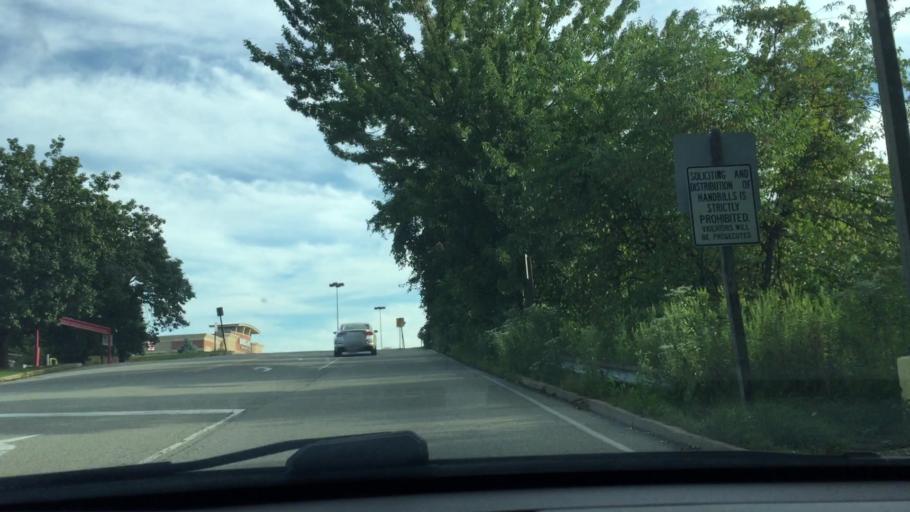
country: US
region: Pennsylvania
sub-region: Allegheny County
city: Monroeville
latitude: 40.4322
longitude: -79.7956
